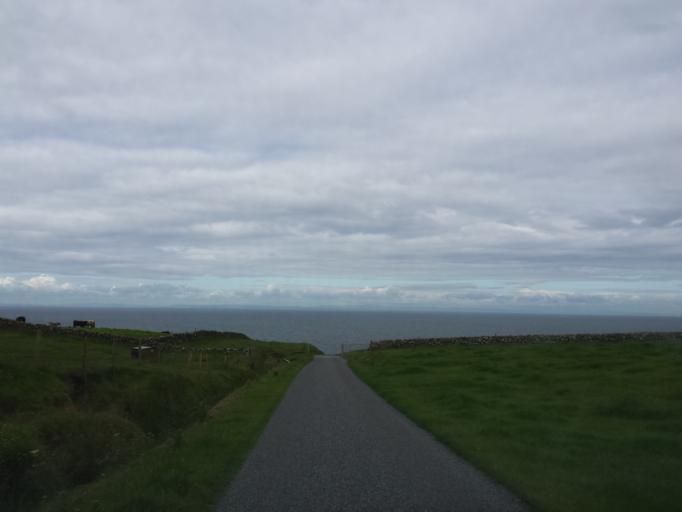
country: GB
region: Scotland
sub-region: Dumfries and Galloway
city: Stranraer
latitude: 54.8657
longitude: -5.1375
